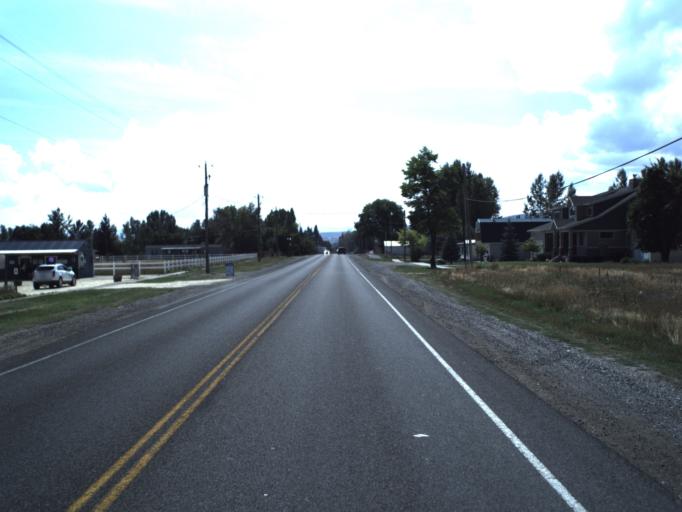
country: US
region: Idaho
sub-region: Bear Lake County
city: Paris
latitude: 41.9421
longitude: -111.3935
